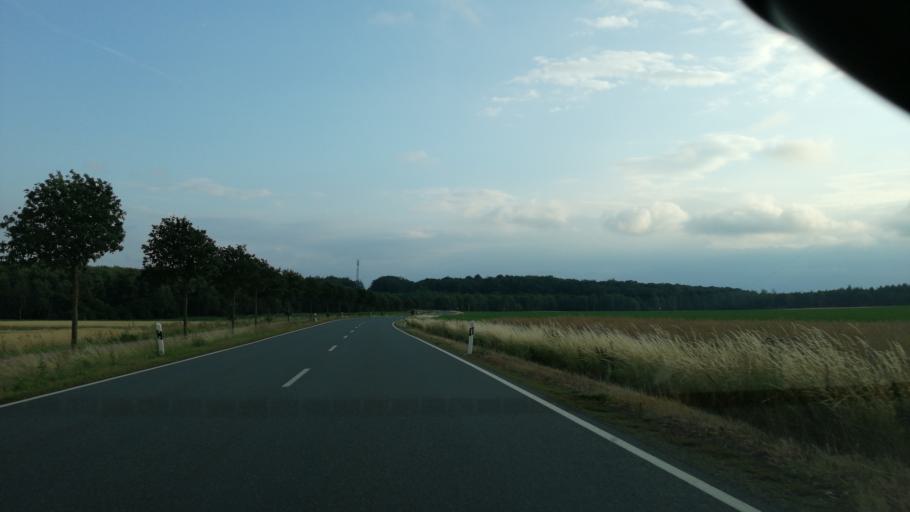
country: DE
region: Saxony-Anhalt
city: Blankenheim
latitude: 51.5421
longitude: 11.3920
